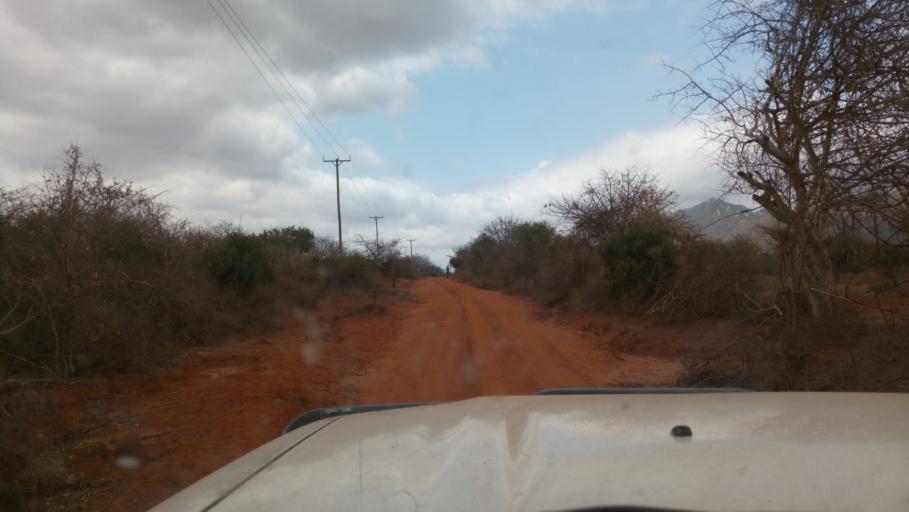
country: KE
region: Kitui
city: Kitui
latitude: -1.8430
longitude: 38.3389
